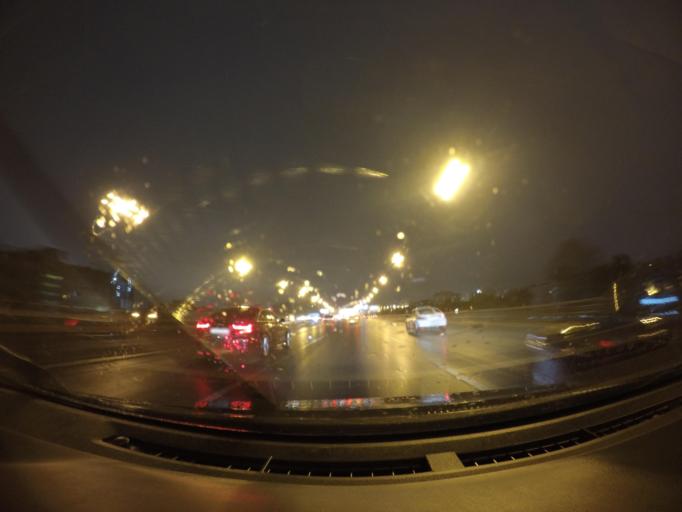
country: RU
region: Moscow
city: Lefortovo
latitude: 55.7289
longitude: 37.7080
